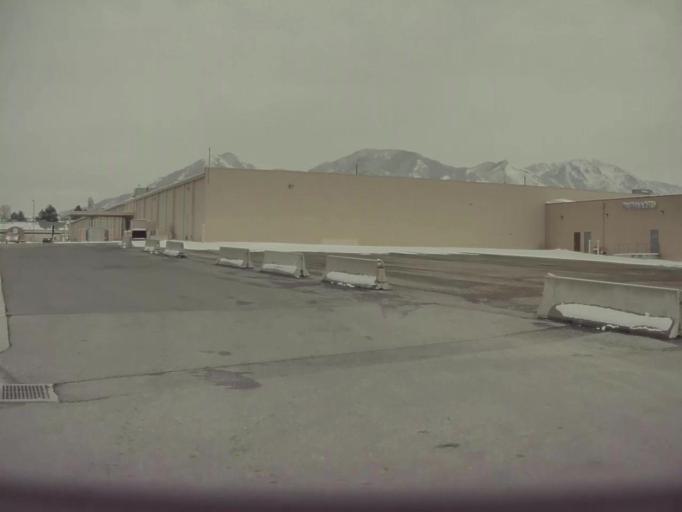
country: US
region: Utah
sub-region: Utah County
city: Spanish Fork
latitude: 40.1233
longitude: -111.6400
